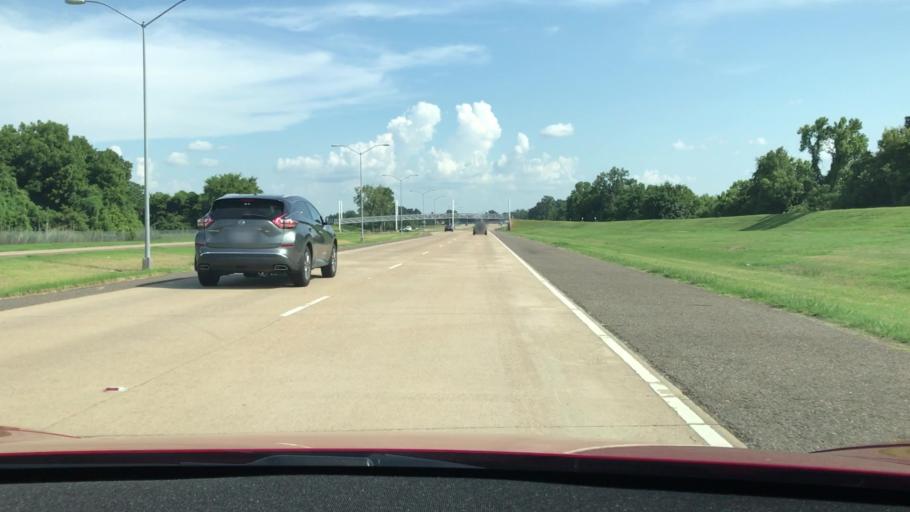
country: US
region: Louisiana
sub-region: Bossier Parish
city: Bossier City
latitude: 32.4723
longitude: -93.6784
